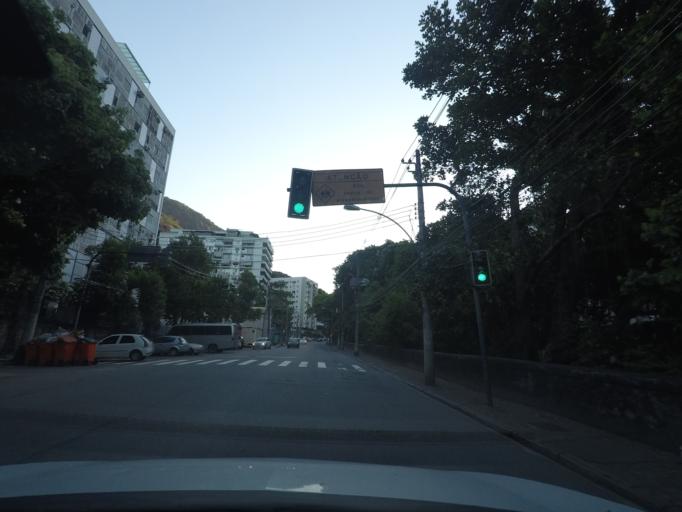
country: BR
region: Rio de Janeiro
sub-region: Rio De Janeiro
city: Rio de Janeiro
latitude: -22.9455
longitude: -43.2548
